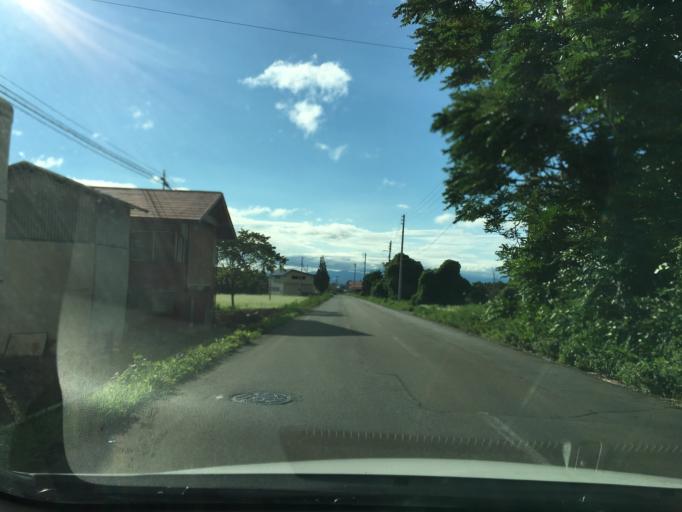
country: JP
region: Yamagata
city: Takahata
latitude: 37.9531
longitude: 140.2016
